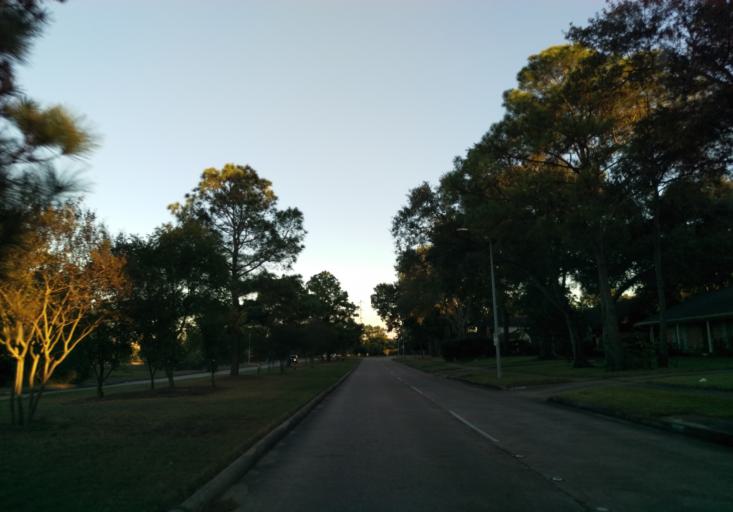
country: US
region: Texas
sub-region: Harris County
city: Spring Valley
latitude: 29.8067
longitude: -95.4383
